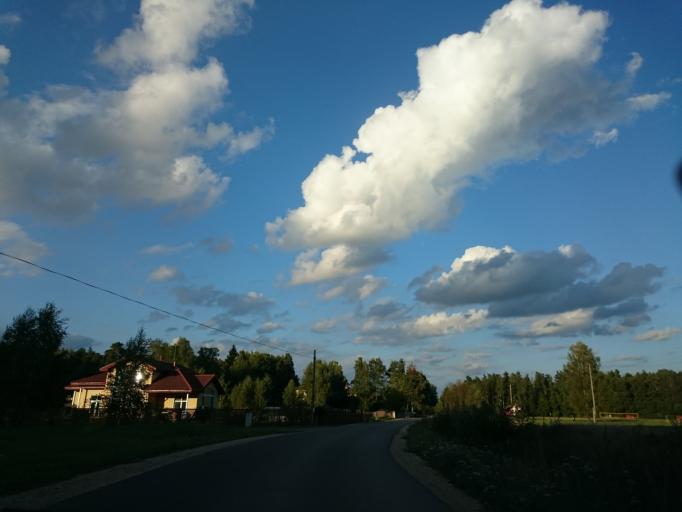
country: LV
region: Adazi
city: Adazi
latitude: 57.0697
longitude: 24.2708
